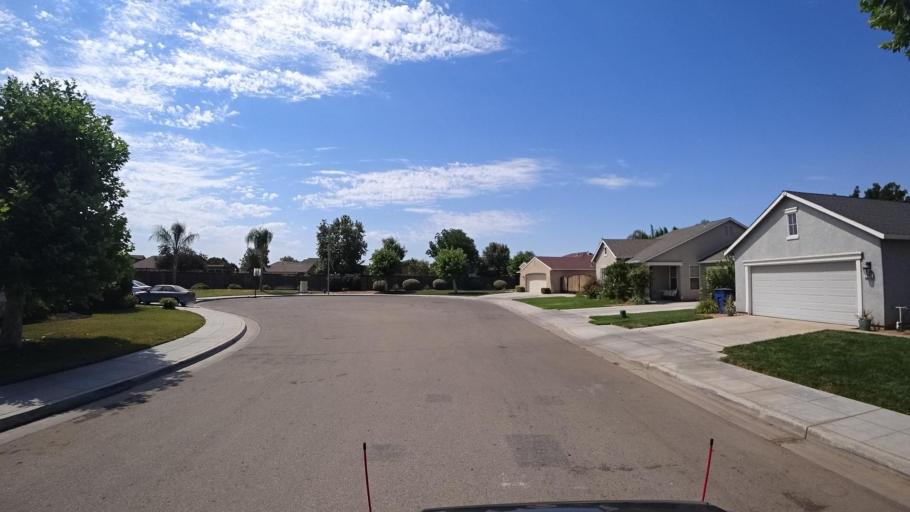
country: US
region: California
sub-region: Fresno County
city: Sunnyside
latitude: 36.7180
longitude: -119.7135
